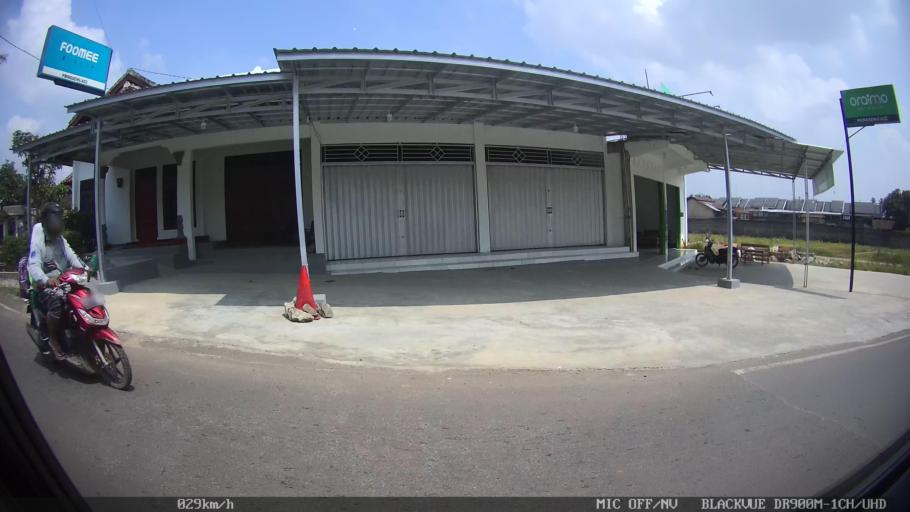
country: ID
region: Lampung
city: Pringsewu
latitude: -5.3668
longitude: 104.9702
